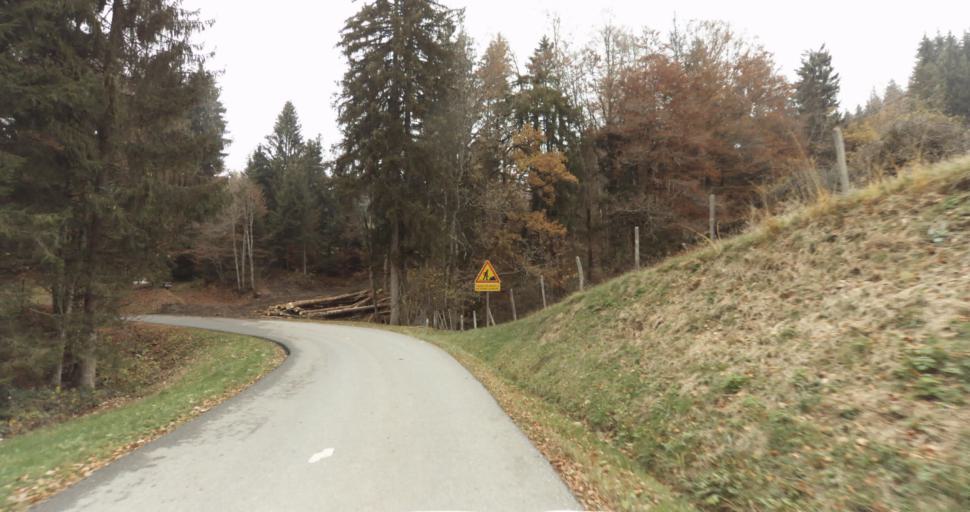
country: FR
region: Rhone-Alpes
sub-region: Departement de la Haute-Savoie
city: Saint-Jorioz
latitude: 45.7569
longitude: 6.1377
